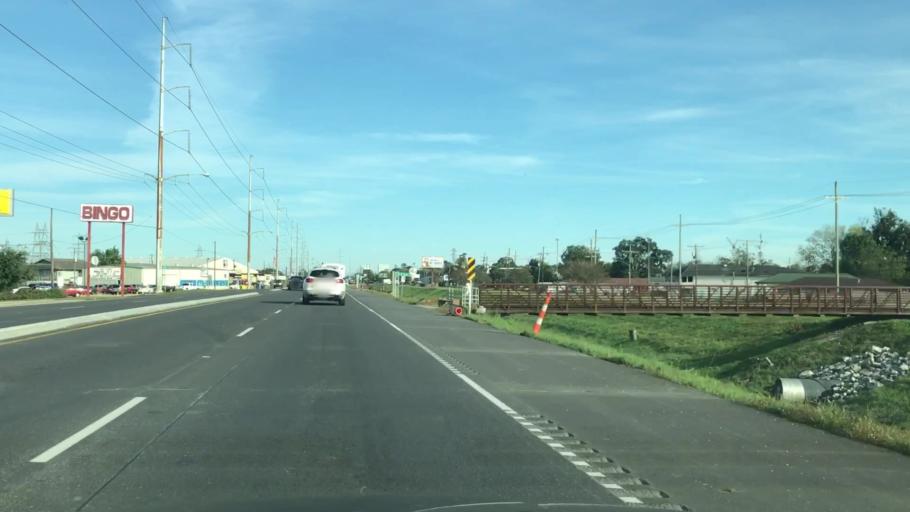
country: US
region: Louisiana
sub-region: Jefferson Parish
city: River Ridge
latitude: 29.9782
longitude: -90.2180
